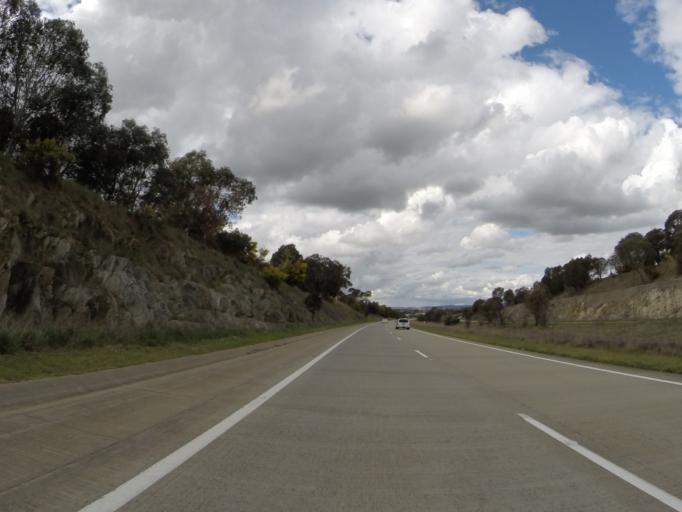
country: AU
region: New South Wales
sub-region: Yass Valley
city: Gundaroo
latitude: -34.7853
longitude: 149.2450
